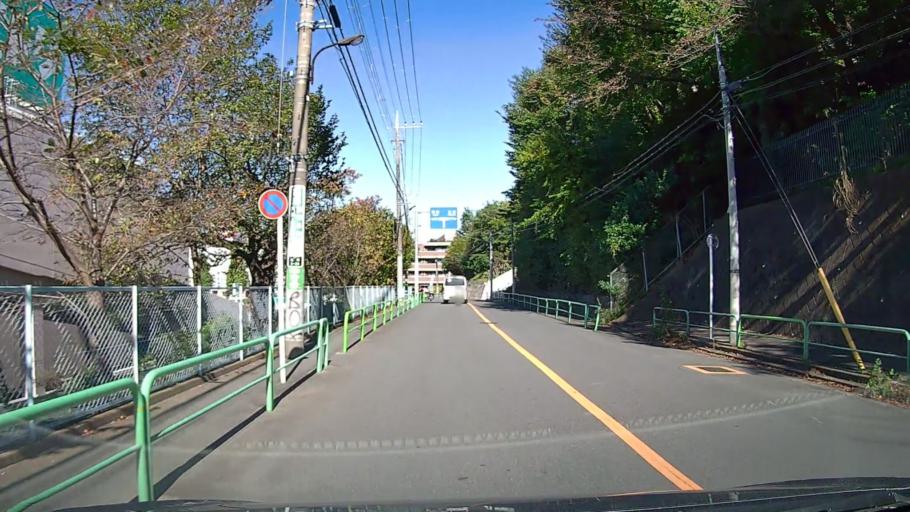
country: JP
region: Saitama
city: Wako
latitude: 35.7782
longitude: 139.6254
